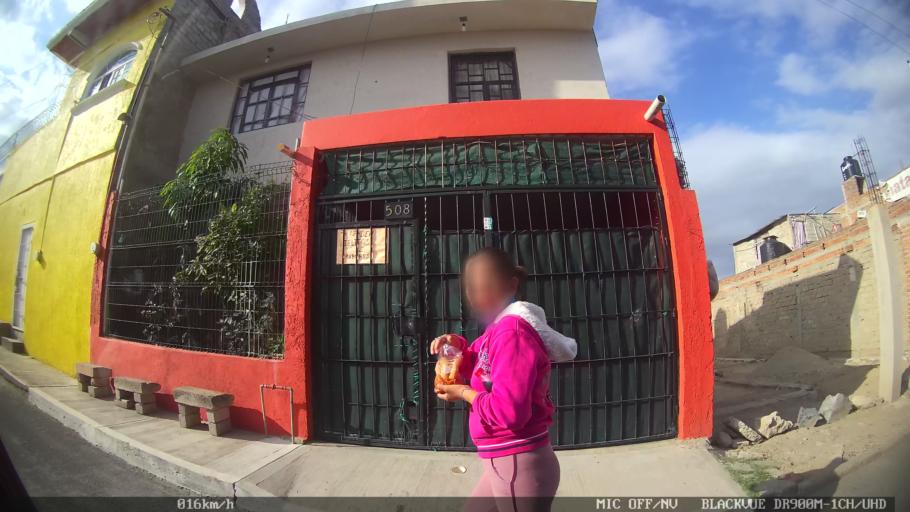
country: MX
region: Jalisco
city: Tonala
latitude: 20.6716
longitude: -103.2409
